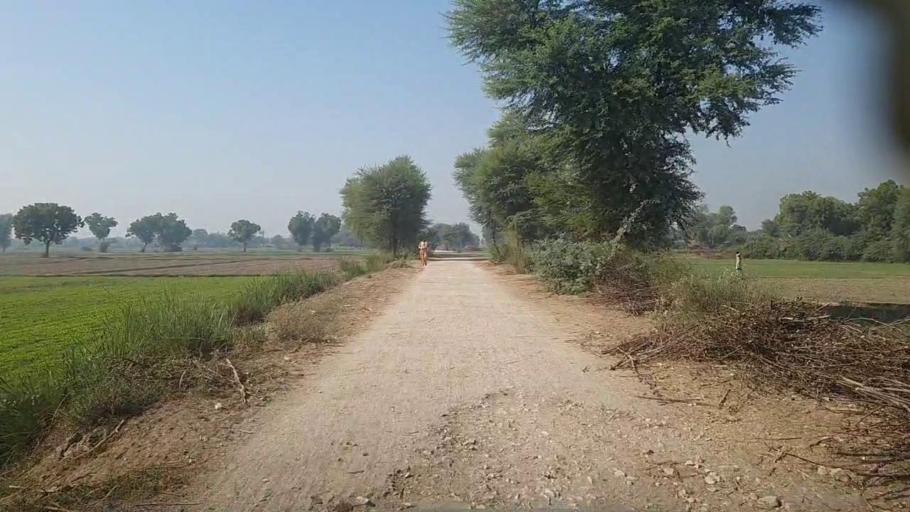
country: PK
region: Sindh
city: Kandiari
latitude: 26.9942
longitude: 68.4841
